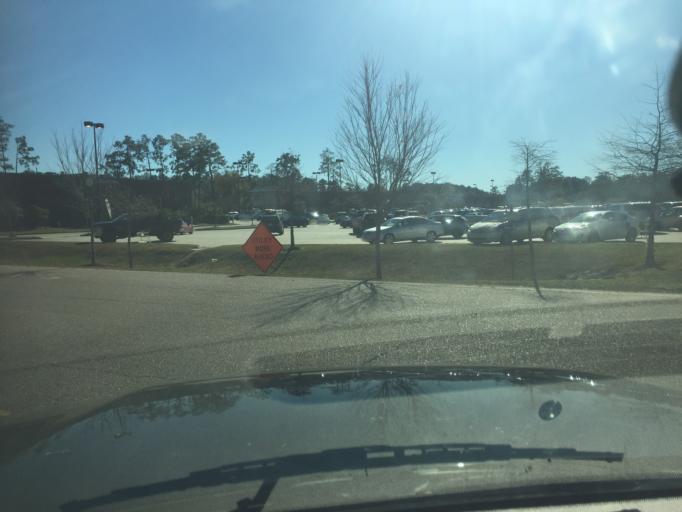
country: US
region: Louisiana
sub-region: Saint Tammany Parish
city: Covington
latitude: 30.4541
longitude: -90.1367
